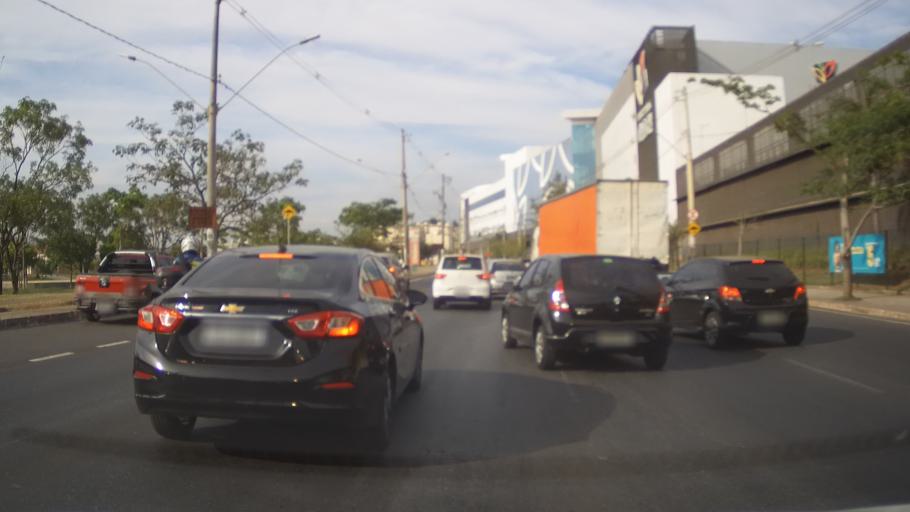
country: BR
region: Minas Gerais
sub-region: Contagem
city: Contagem
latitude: -19.8794
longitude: -44.0367
